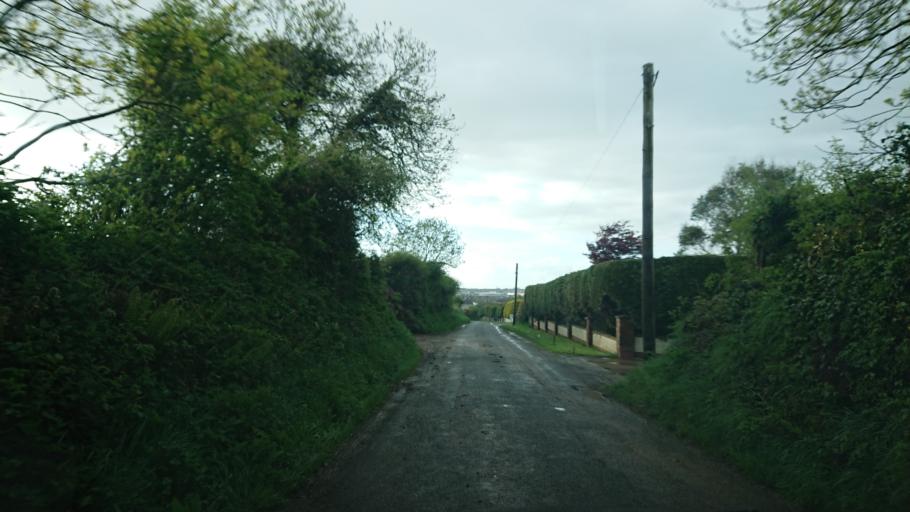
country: IE
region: Munster
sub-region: Waterford
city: Waterford
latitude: 52.2354
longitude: -7.1313
